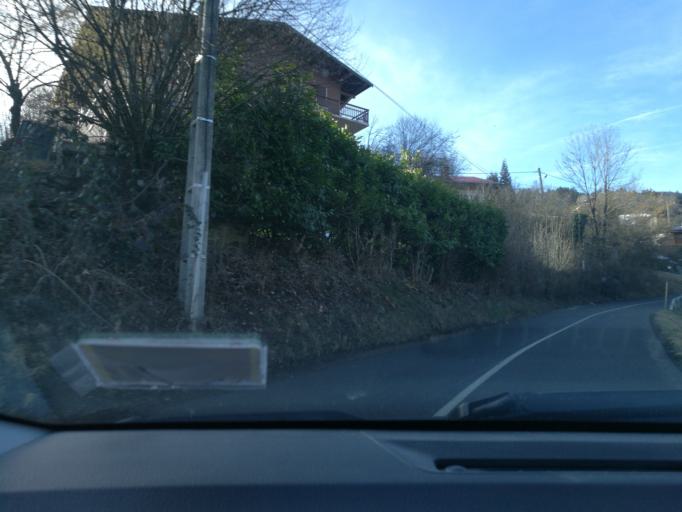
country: FR
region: Rhone-Alpes
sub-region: Departement de la Haute-Savoie
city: Saint-Gervais-les-Bains
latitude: 45.9017
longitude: 6.7009
